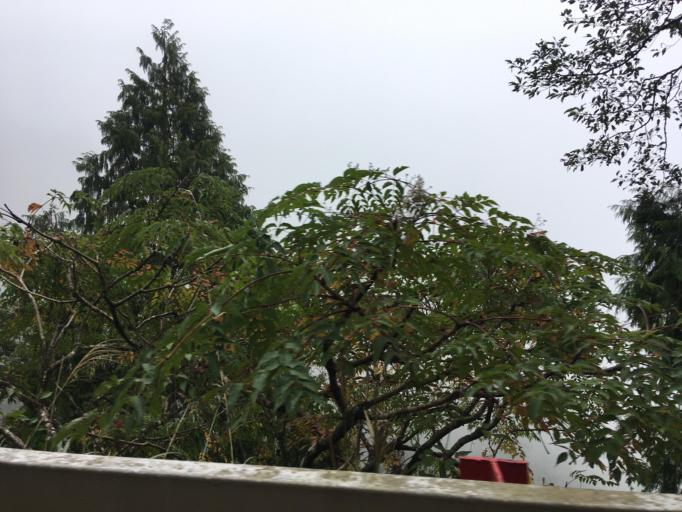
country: TW
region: Taiwan
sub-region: Yilan
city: Yilan
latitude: 24.4818
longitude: 121.5361
